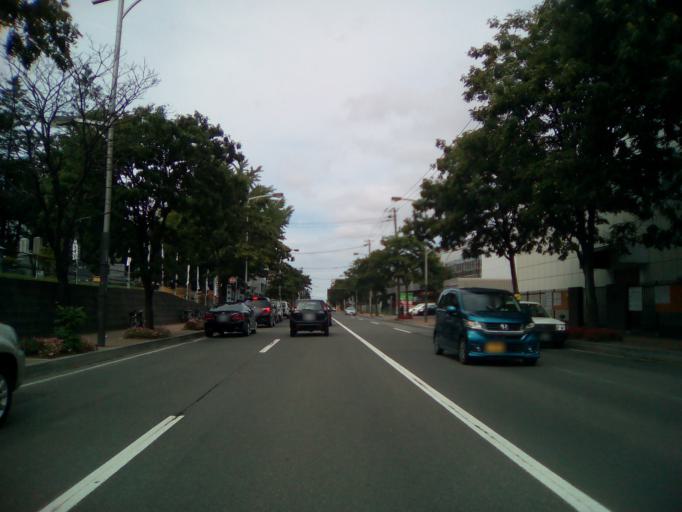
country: JP
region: Hokkaido
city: Sapporo
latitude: 43.0201
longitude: 141.3670
